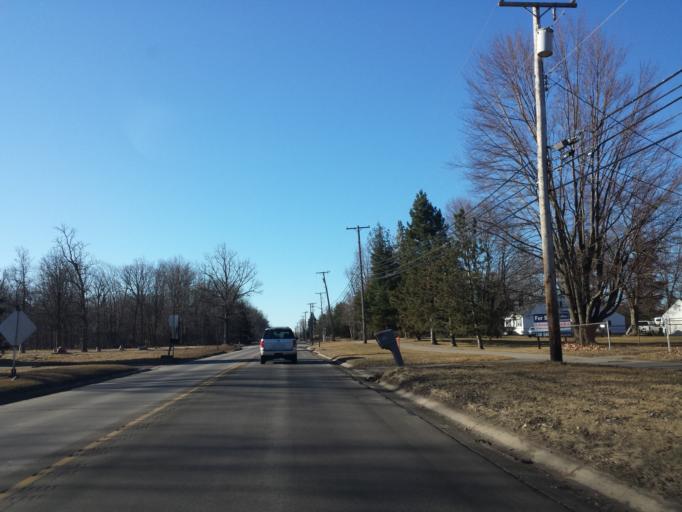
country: US
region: Michigan
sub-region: Oakland County
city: Rochester Hills
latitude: 42.6492
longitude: -83.1527
